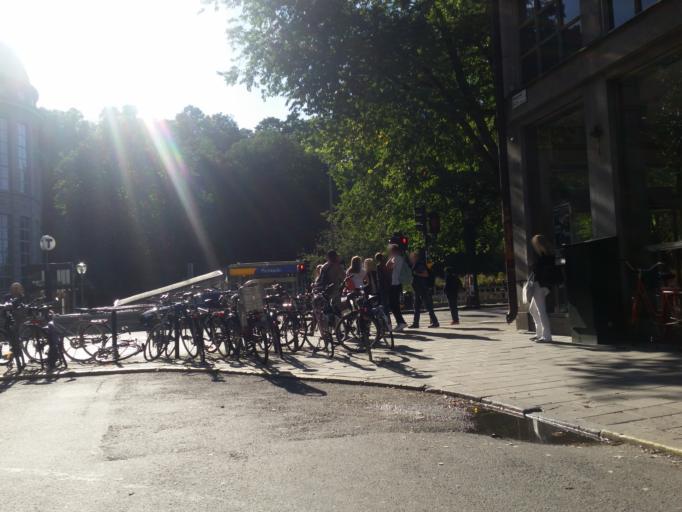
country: SE
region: Stockholm
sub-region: Stockholms Kommun
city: Stockholm
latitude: 59.3424
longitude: 18.0579
